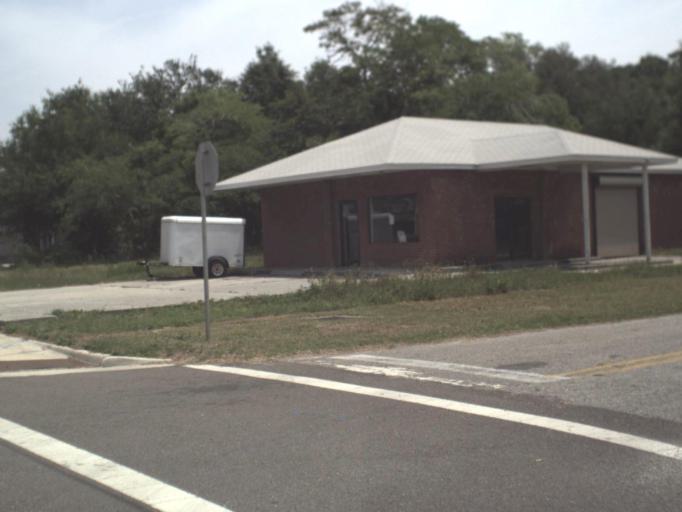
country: US
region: Florida
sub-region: Nassau County
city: Fernandina Beach
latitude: 30.6594
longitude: -81.4605
